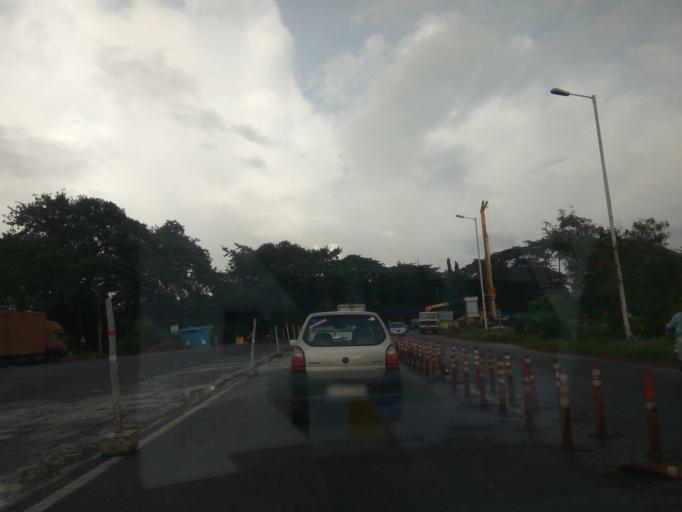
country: IN
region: Goa
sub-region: South Goa
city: Cortalim
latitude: 15.4233
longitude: 73.8999
